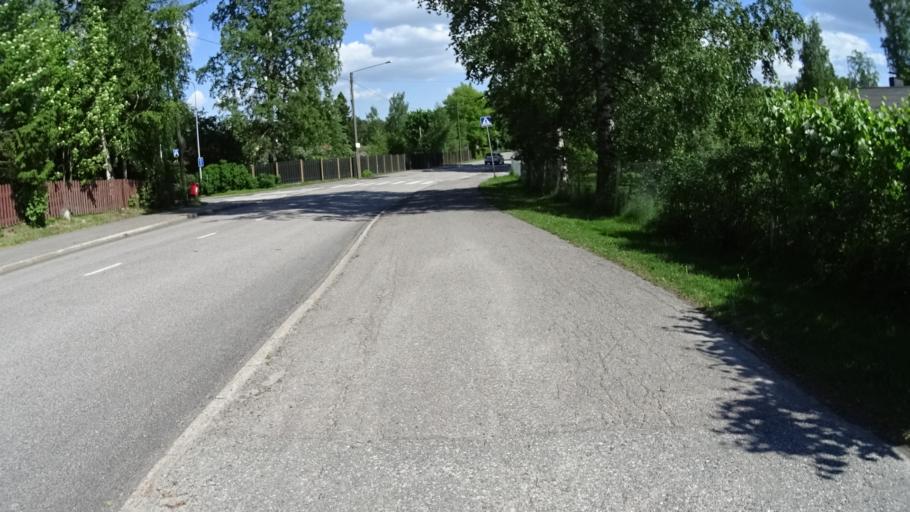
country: FI
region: Uusimaa
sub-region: Helsinki
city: Kilo
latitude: 60.1999
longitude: 24.7585
